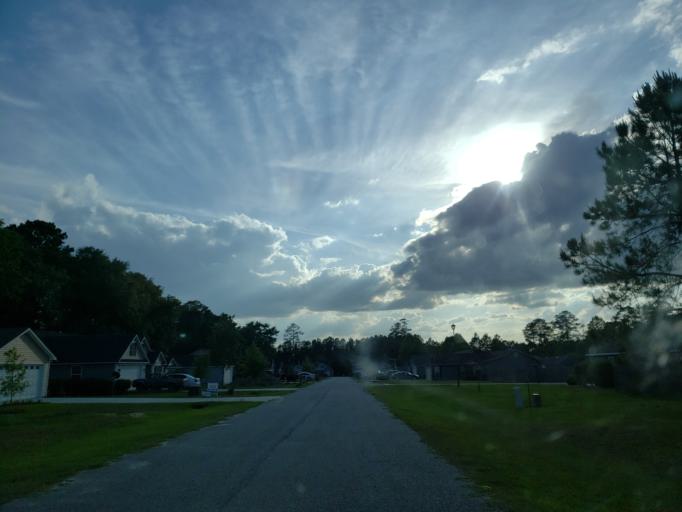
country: US
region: Georgia
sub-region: Cook County
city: Adel
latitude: 31.1244
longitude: -83.4135
